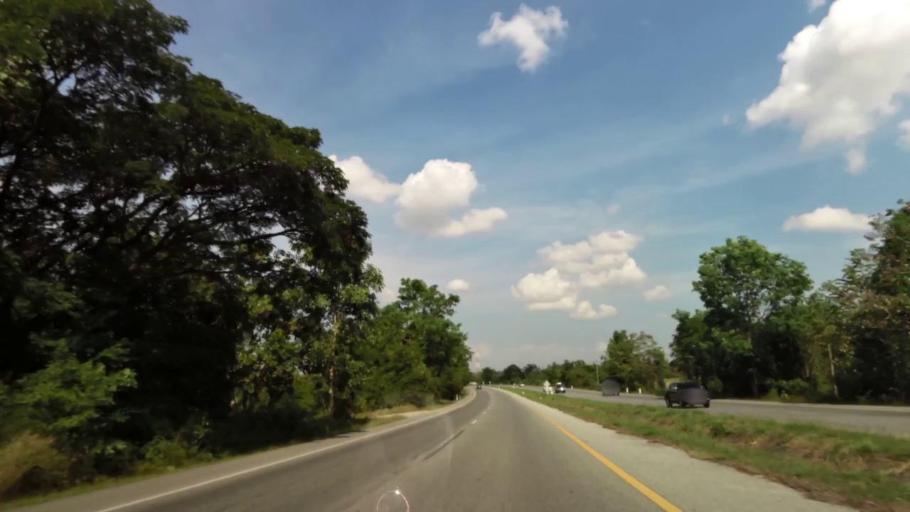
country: TH
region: Uttaradit
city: Thong Saen Khan
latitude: 17.4581
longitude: 100.2378
